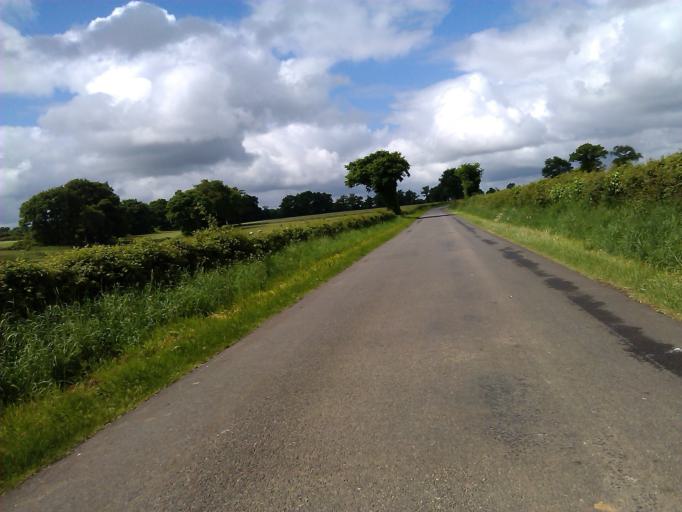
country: FR
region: Poitou-Charentes
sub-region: Departement de la Vienne
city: Availles-Limouzine
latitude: 46.1106
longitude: 0.5601
